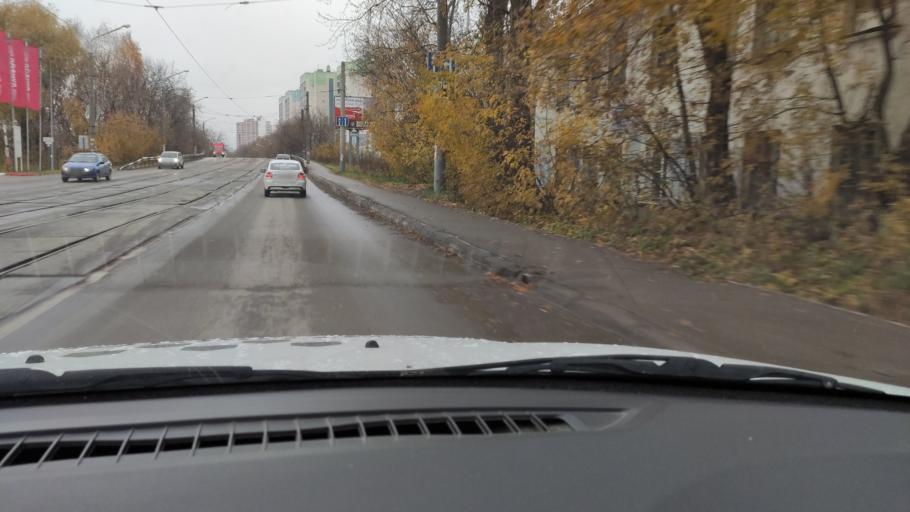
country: RU
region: Perm
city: Perm
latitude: 57.9911
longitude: 56.2181
